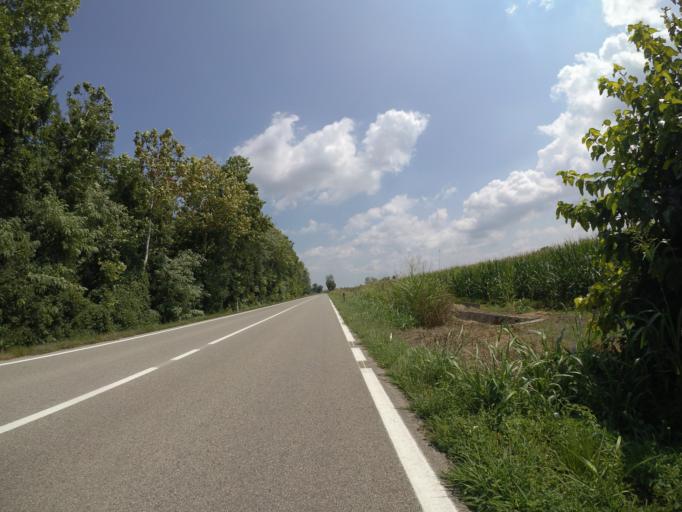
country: IT
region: Friuli Venezia Giulia
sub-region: Provincia di Udine
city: Sedegliano
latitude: 46.0168
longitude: 12.9917
